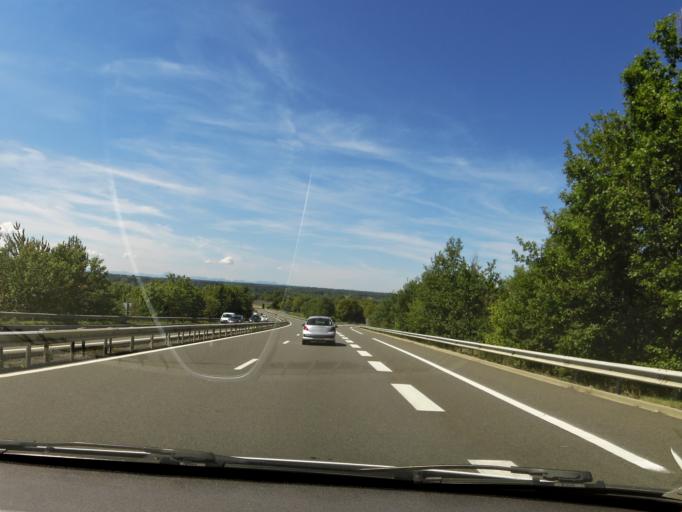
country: FR
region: Auvergne
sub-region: Departement du Puy-de-Dome
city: Peschadoires
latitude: 45.8616
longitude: 3.5065
